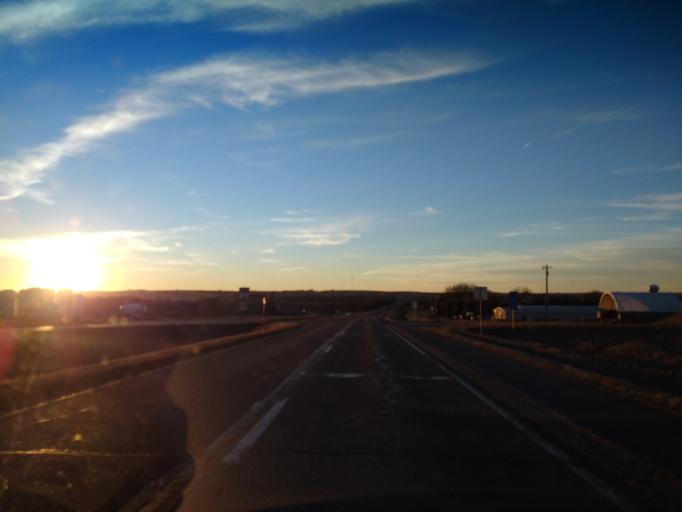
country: US
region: Iowa
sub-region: Woodbury County
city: Moville
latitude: 42.4820
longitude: -96.0553
